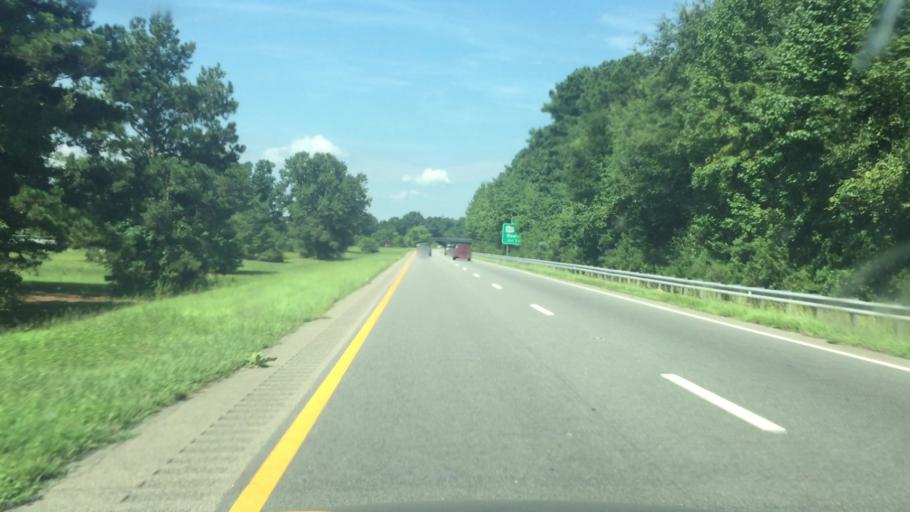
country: US
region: North Carolina
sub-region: Scotland County
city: Laurinburg
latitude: 34.7559
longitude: -79.4394
